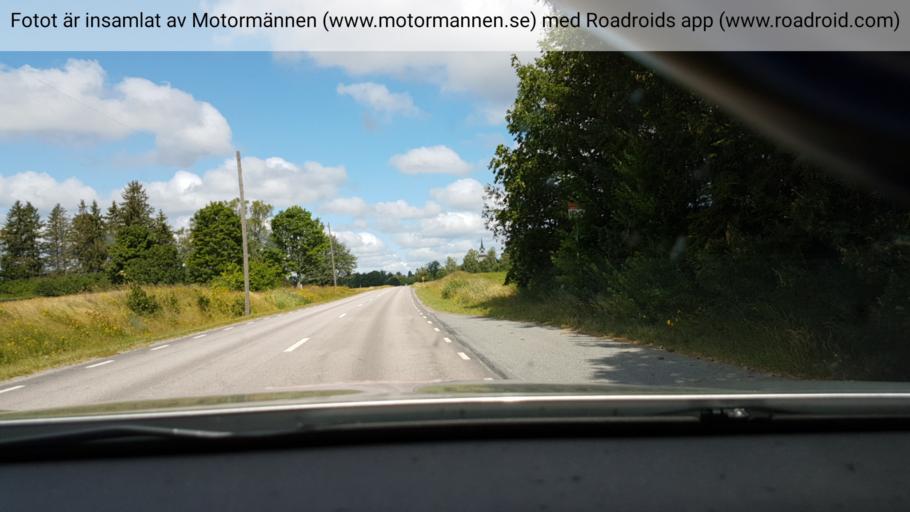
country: SE
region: Stockholm
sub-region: Norrtalje Kommun
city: Hallstavik
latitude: 59.9826
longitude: 18.8129
